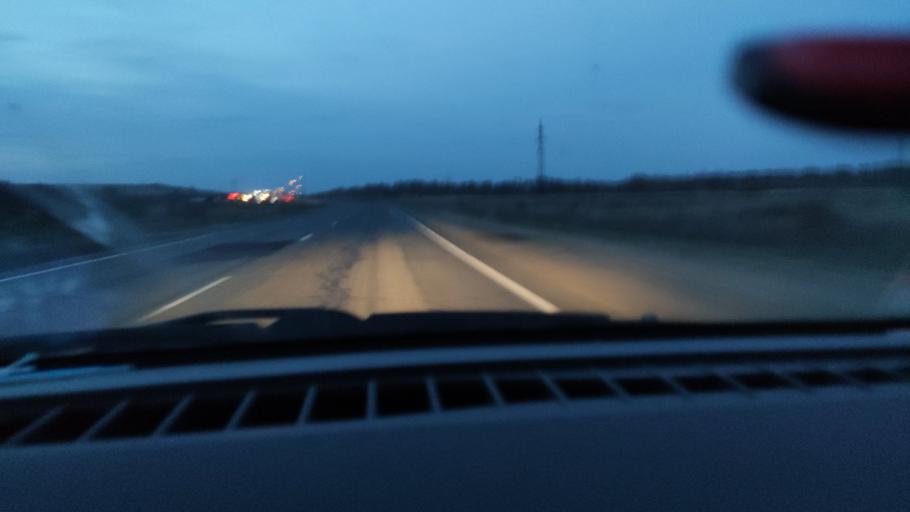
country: RU
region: Saratov
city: Sinodskoye
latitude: 52.0814
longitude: 46.7961
